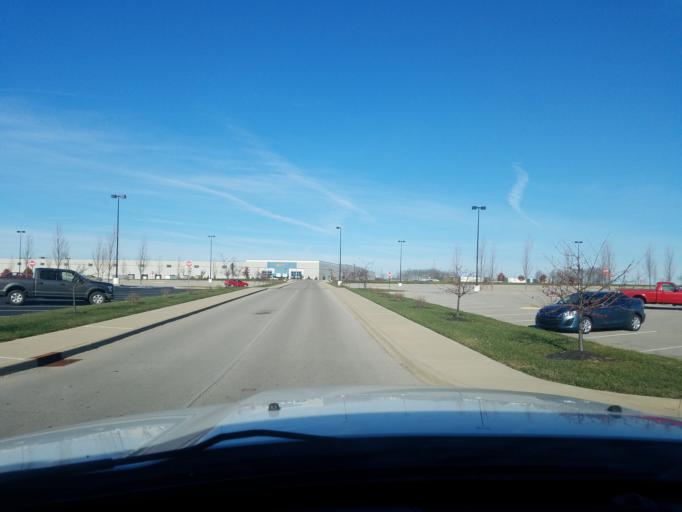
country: US
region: Indiana
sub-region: Clark County
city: Sellersburg
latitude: 38.3798
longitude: -85.6843
